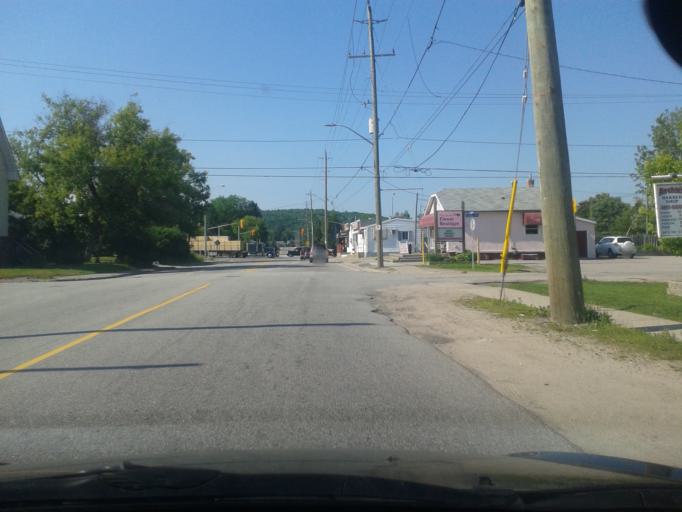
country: CA
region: Ontario
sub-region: Nipissing District
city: North Bay
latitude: 46.3269
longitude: -79.4572
